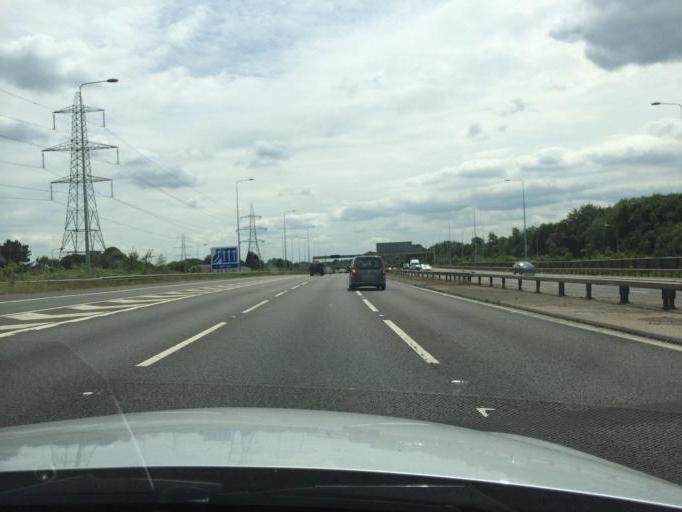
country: GB
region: England
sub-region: Trafford
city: Sale
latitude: 53.4270
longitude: -2.2940
